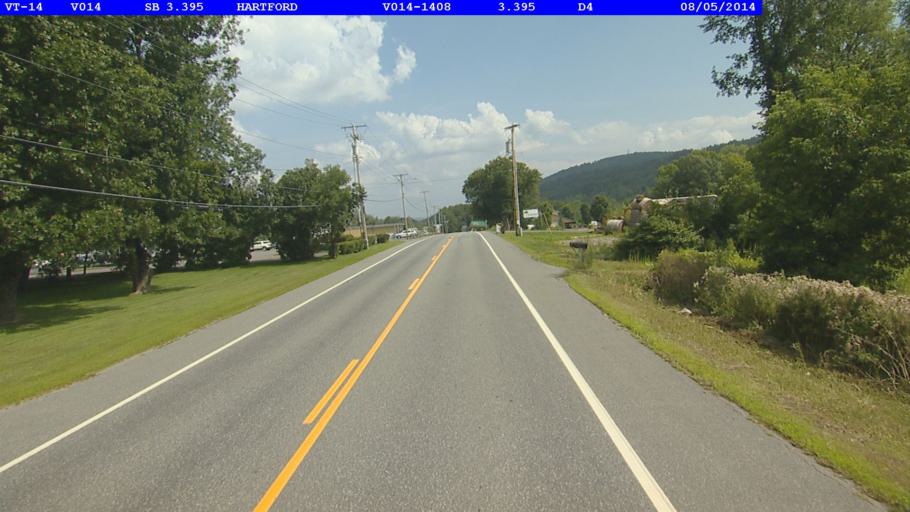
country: US
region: Vermont
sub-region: Windsor County
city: White River Junction
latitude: 43.6725
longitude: -72.3793
